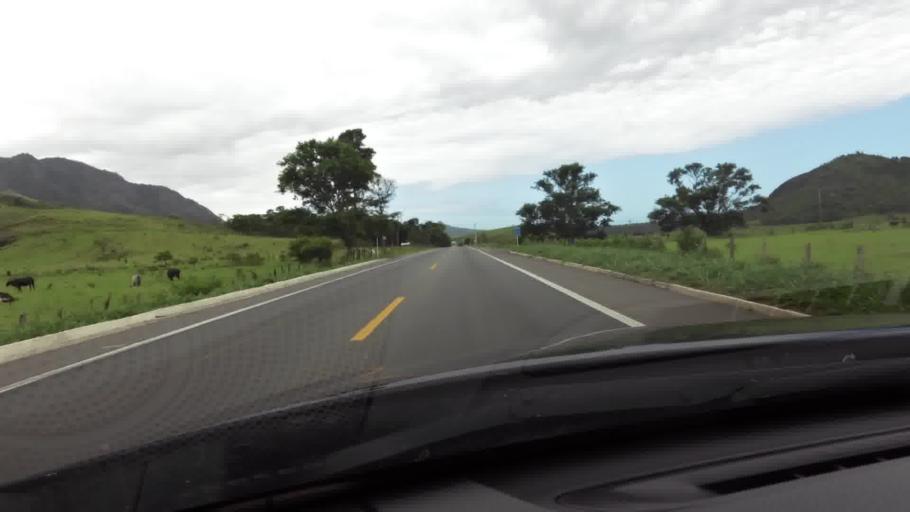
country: BR
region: Espirito Santo
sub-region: Guarapari
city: Guarapari
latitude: -20.6151
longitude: -40.5145
